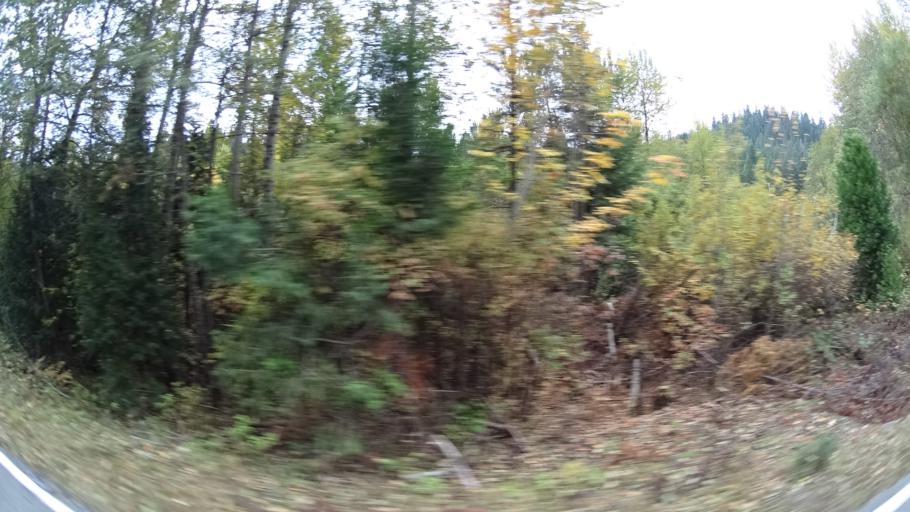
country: US
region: California
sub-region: Siskiyou County
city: Happy Camp
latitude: 41.9149
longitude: -123.4636
